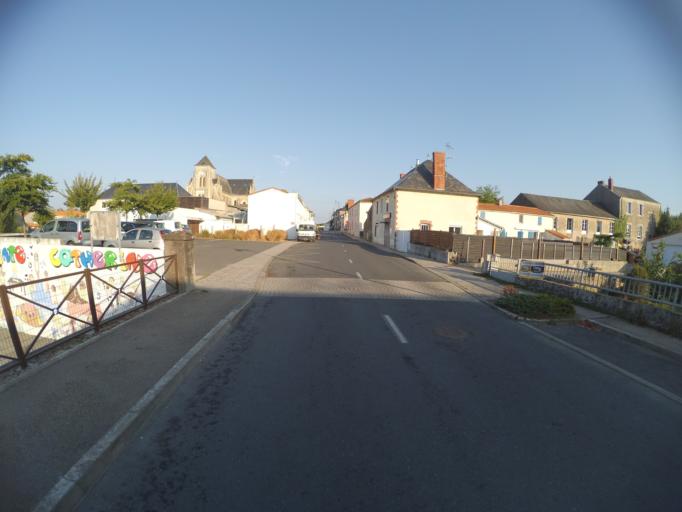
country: FR
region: Pays de la Loire
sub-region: Departement de la Loire-Atlantique
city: La Planche
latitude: 47.0162
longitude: -1.4346
